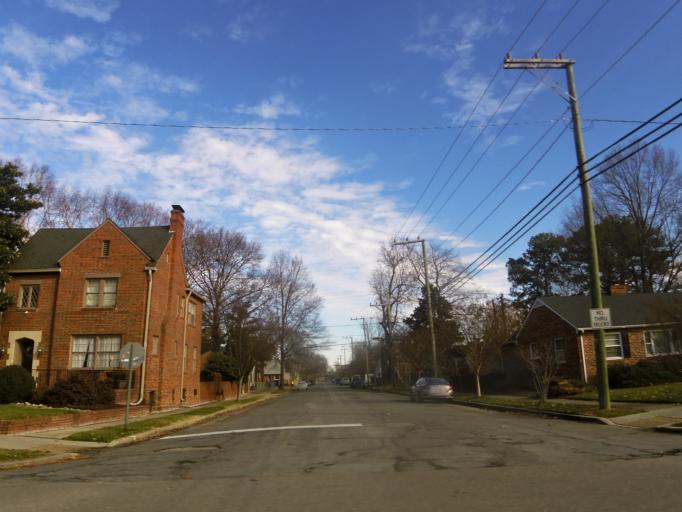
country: US
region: Virginia
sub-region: City of Richmond
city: Richmond
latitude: 37.5688
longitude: -77.4849
